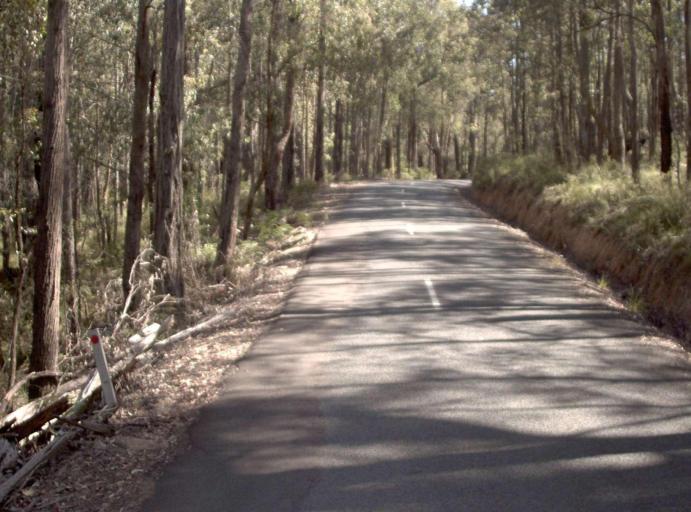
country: AU
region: New South Wales
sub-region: Bombala
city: Bombala
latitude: -37.3860
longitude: 148.6172
